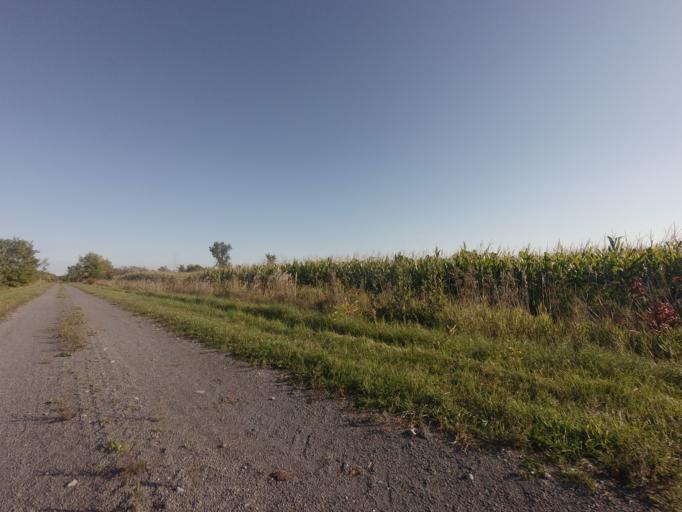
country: CA
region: Ontario
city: Hawkesbury
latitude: 45.5138
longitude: -74.5100
